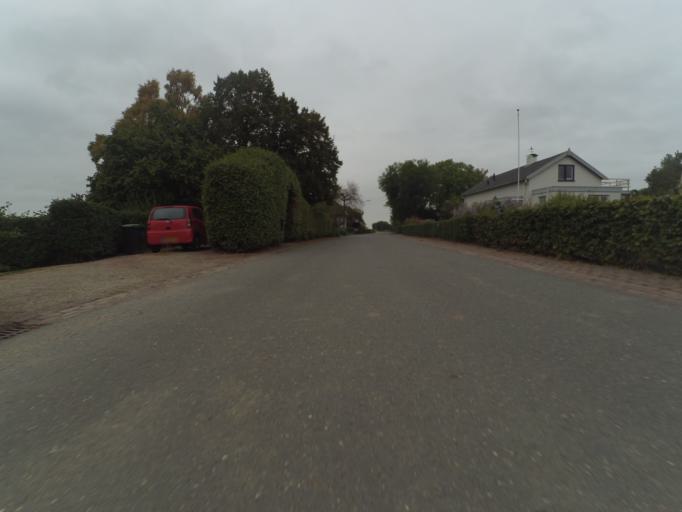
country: NL
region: Gelderland
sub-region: Gemeente Tiel
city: Tiel
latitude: 51.9035
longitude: 5.3730
